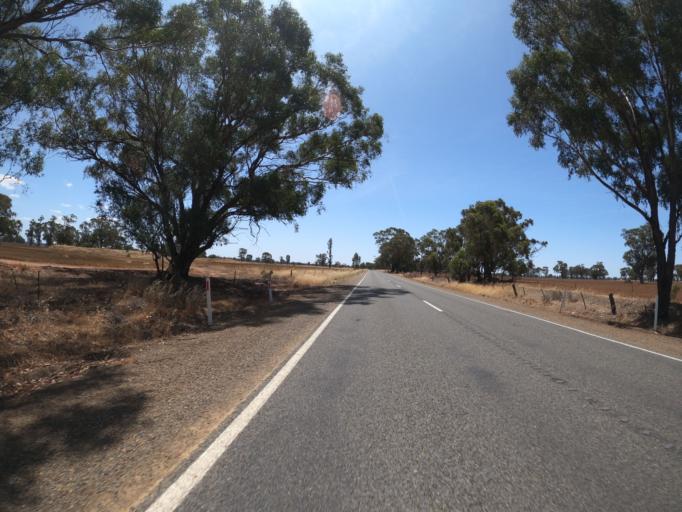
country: AU
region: Victoria
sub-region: Moira
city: Yarrawonga
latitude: -36.2031
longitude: 145.9672
